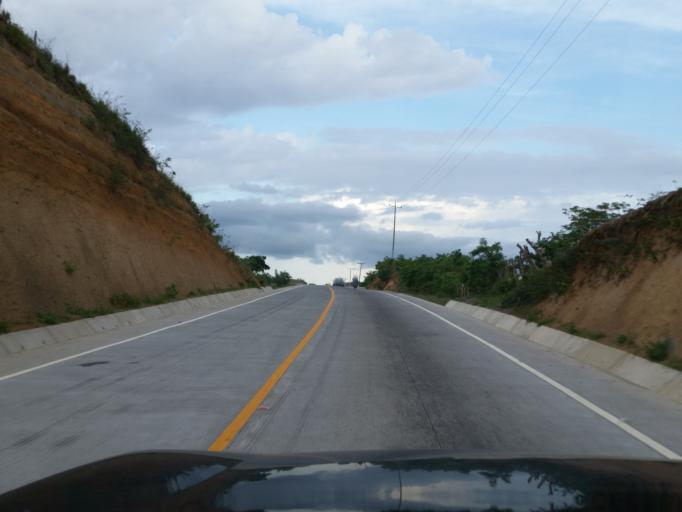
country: NI
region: Managua
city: Carlos Fonseca Amador
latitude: 12.0679
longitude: -86.4424
